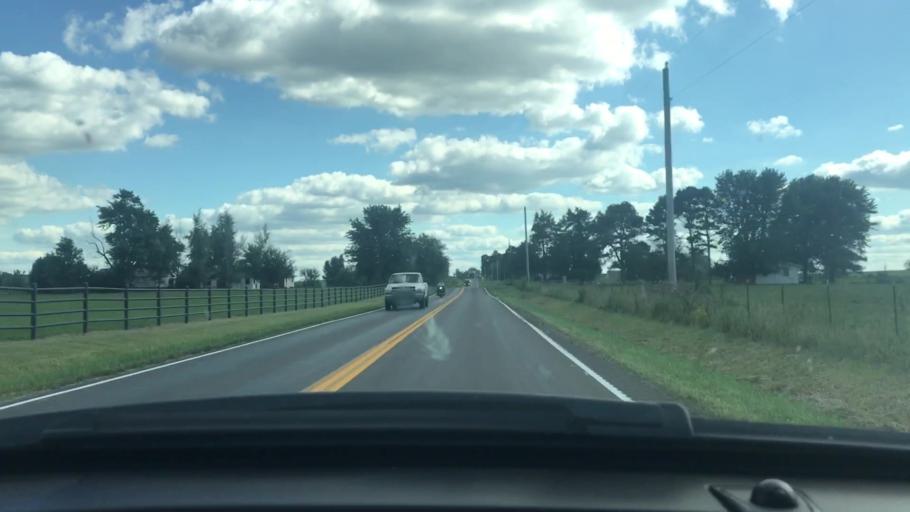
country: US
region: Missouri
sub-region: Wright County
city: Mountain Grove
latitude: 37.1726
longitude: -92.2671
